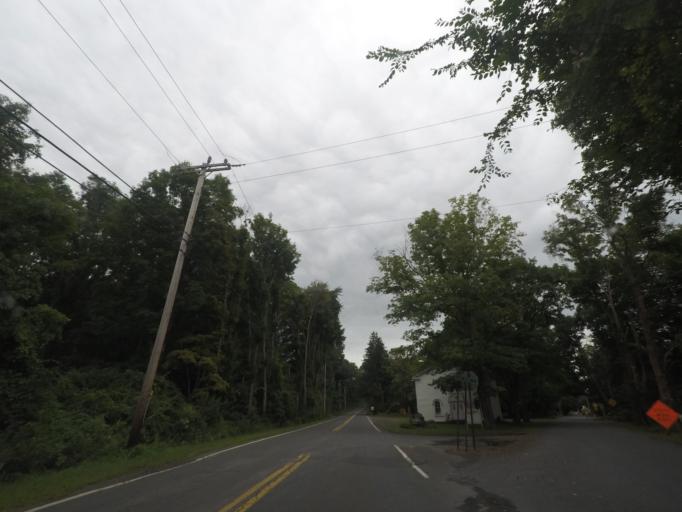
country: US
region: New York
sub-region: Rensselaer County
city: Nassau
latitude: 42.4681
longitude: -73.5814
